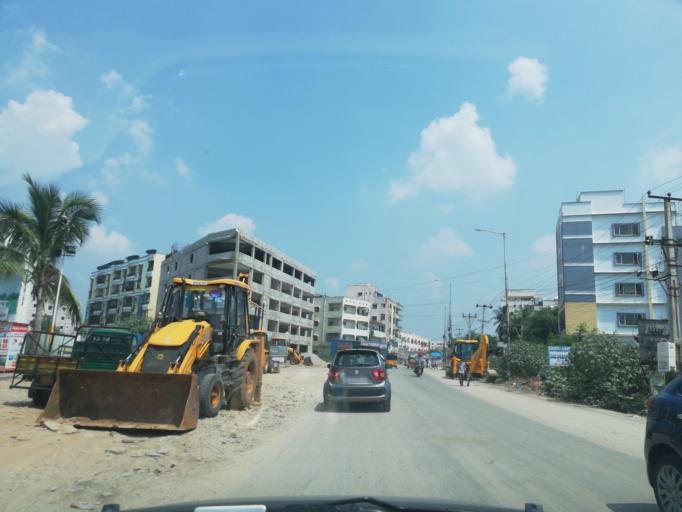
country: IN
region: Telangana
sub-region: Medak
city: Serilingampalle
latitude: 17.4854
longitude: 78.3201
